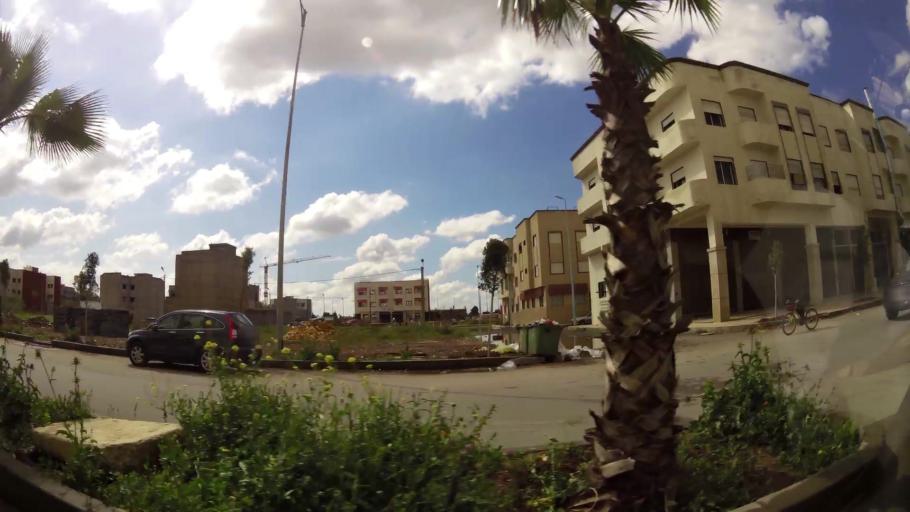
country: MA
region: Grand Casablanca
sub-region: Mediouna
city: Mediouna
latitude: 33.3799
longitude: -7.5350
